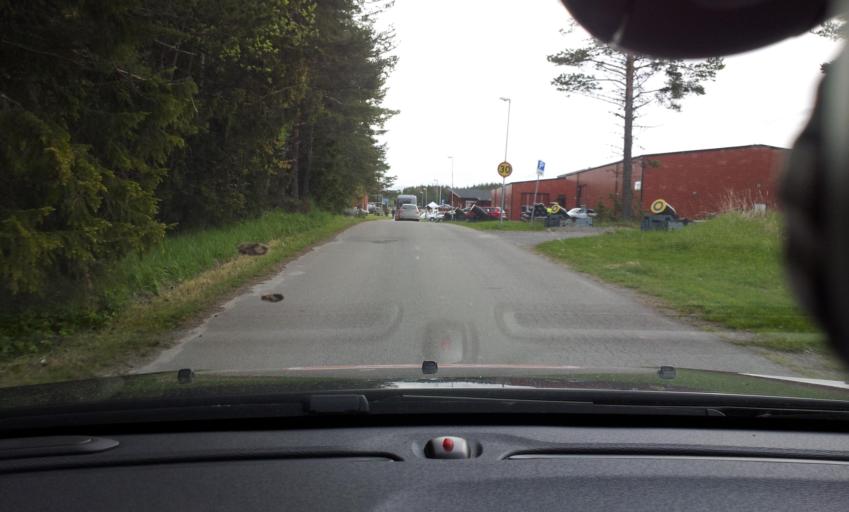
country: SE
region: Jaemtland
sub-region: OEstersunds Kommun
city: Brunflo
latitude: 63.1259
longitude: 14.7953
